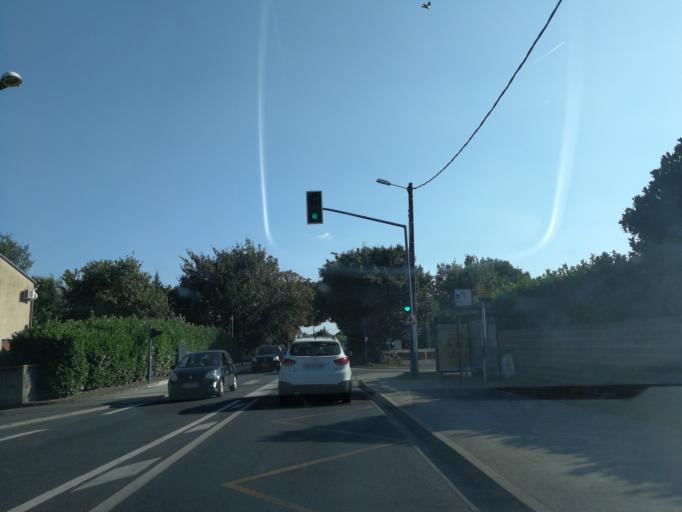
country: FR
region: Midi-Pyrenees
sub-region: Departement de la Haute-Garonne
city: Launaguet
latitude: 43.6707
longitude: 1.4454
